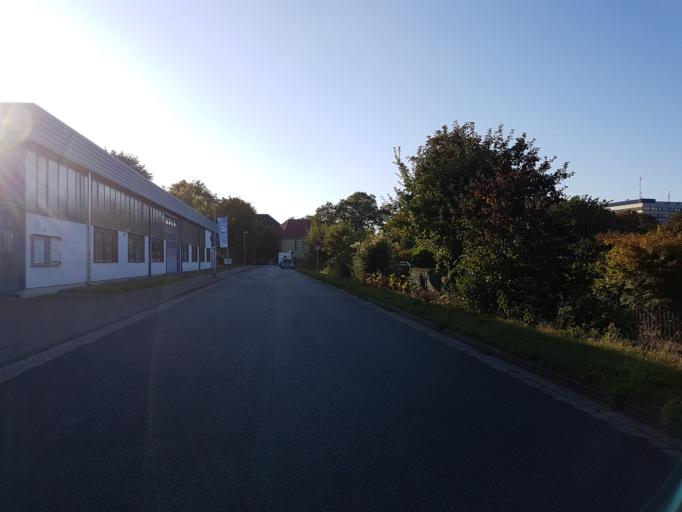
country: DE
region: Lower Saxony
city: Hannover
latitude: 52.4000
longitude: 9.7514
